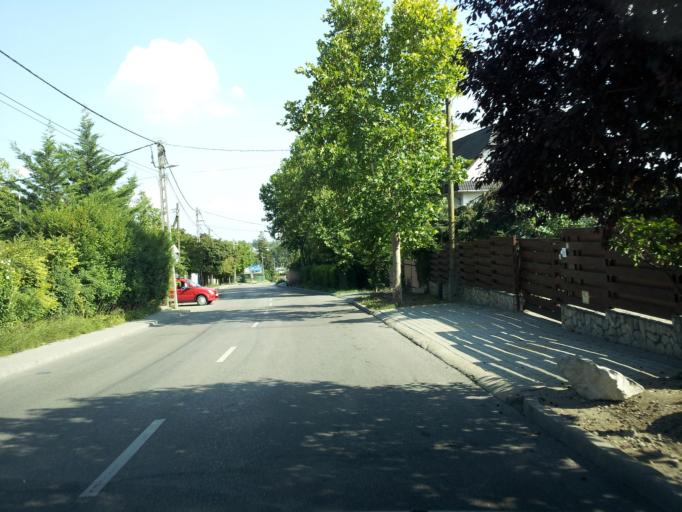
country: HU
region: Budapest
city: Budapest XXII. keruelet
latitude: 47.4145
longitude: 19.0219
